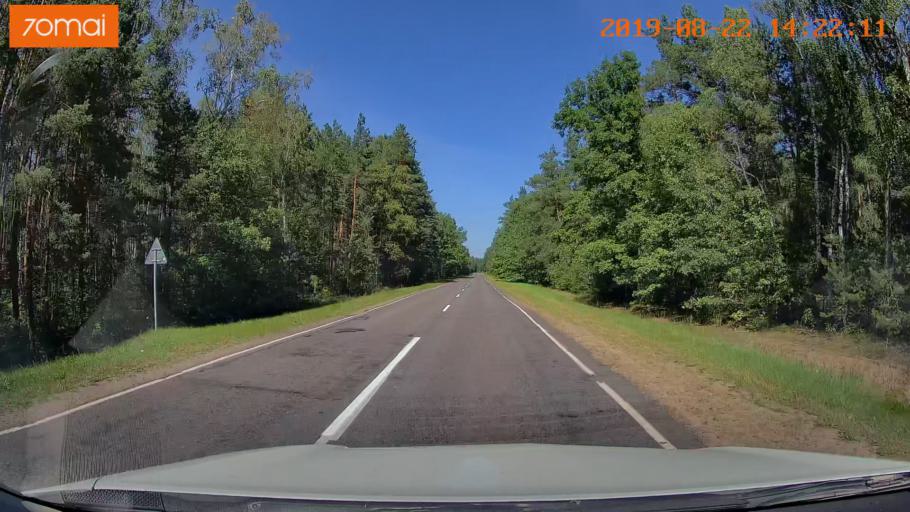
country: BY
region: Mogilev
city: Asipovichy
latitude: 53.2733
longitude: 28.5684
